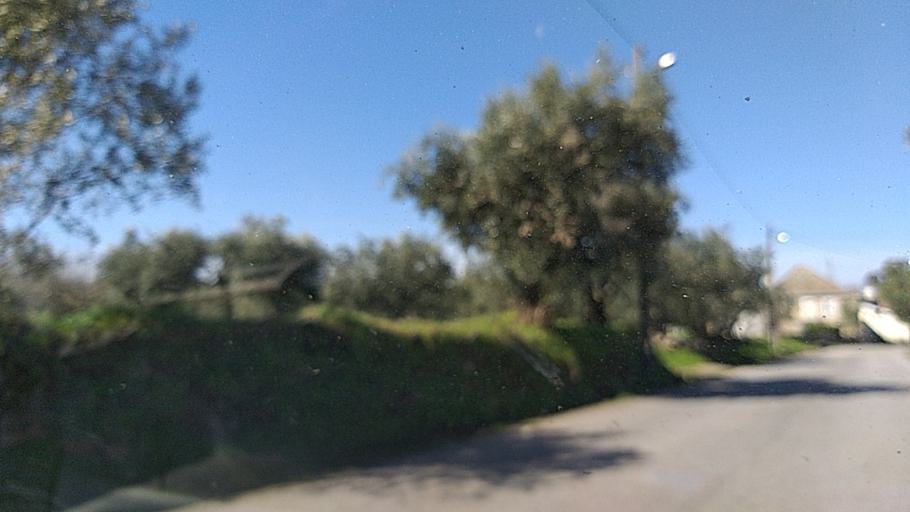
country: PT
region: Guarda
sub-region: Fornos de Algodres
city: Fornos de Algodres
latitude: 40.5930
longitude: -7.4670
